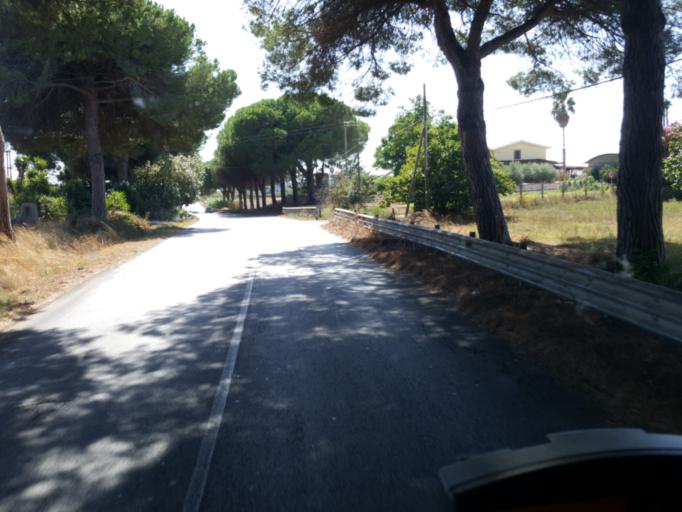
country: IT
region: Latium
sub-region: Citta metropolitana di Roma Capitale
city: Nettuno
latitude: 41.5091
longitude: 12.6919
